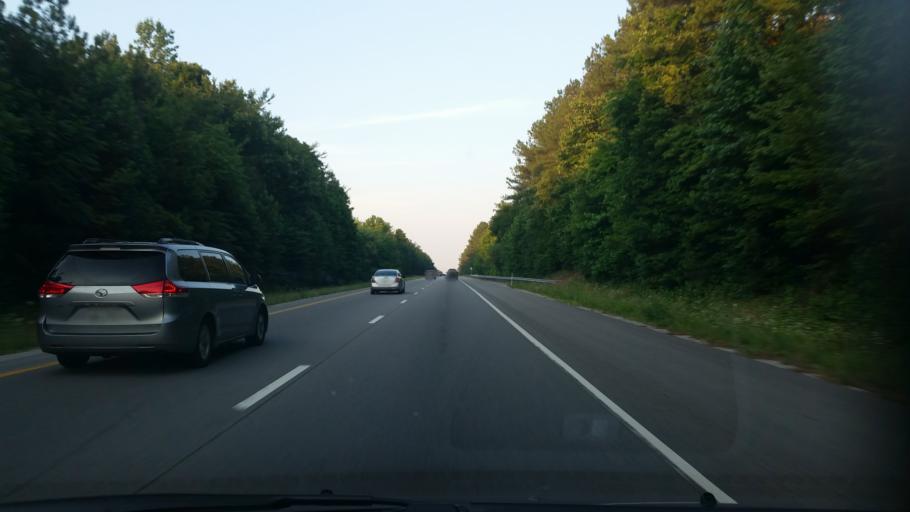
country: US
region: Tennessee
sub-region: Putnam County
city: Baxter
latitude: 36.1259
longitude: -85.6784
